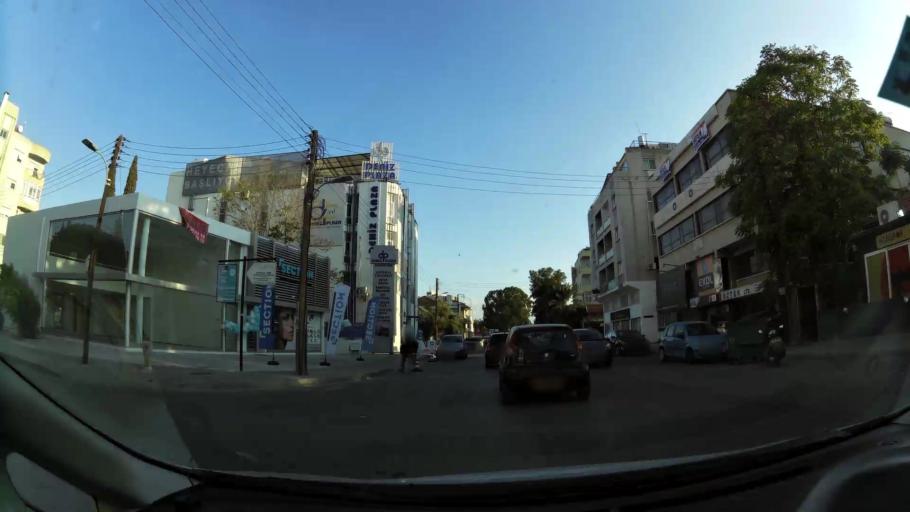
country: CY
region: Lefkosia
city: Nicosia
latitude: 35.1880
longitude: 33.3585
